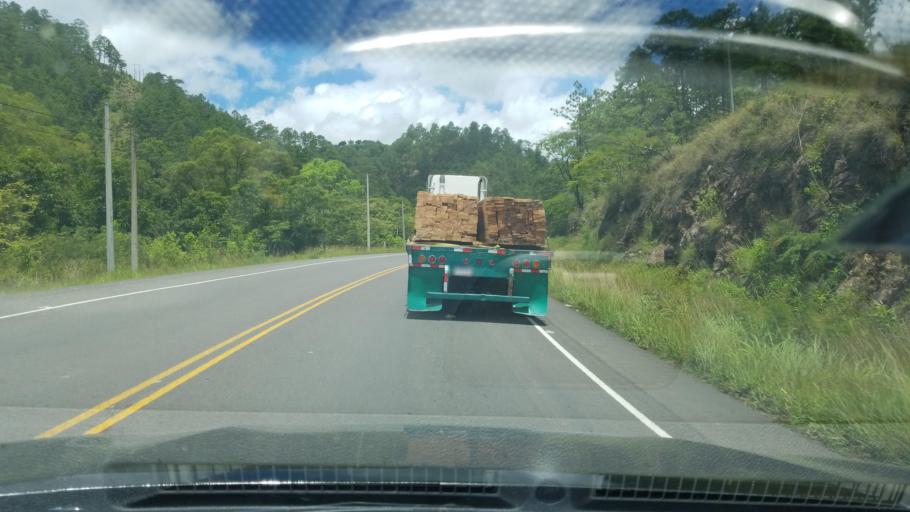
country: HN
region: Francisco Morazan
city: Talanga
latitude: 14.3922
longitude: -87.1297
